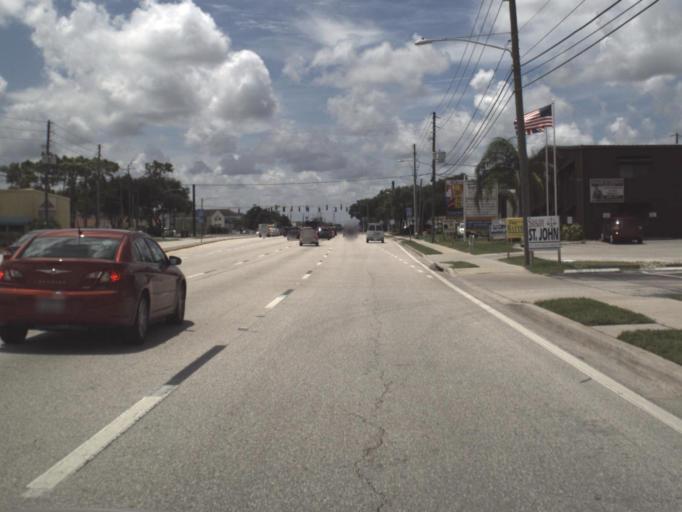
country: US
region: Florida
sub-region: Pinellas County
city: South Highpoint
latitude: 27.8963
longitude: -82.7005
